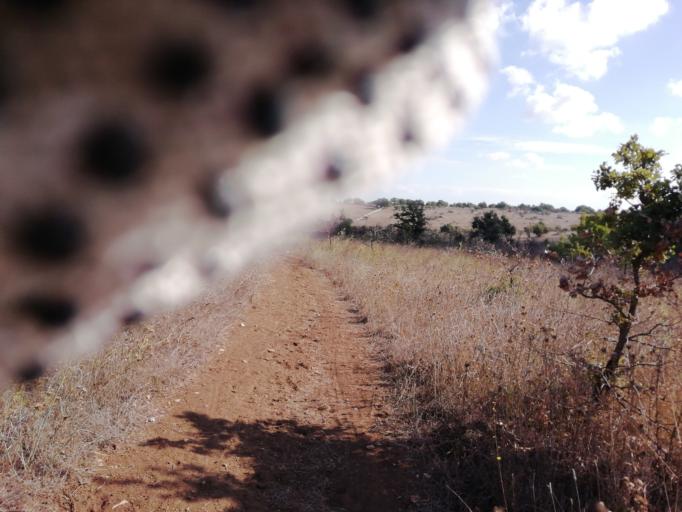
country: IT
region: Apulia
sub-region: Provincia di Bari
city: Corato
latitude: 41.0879
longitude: 16.2833
